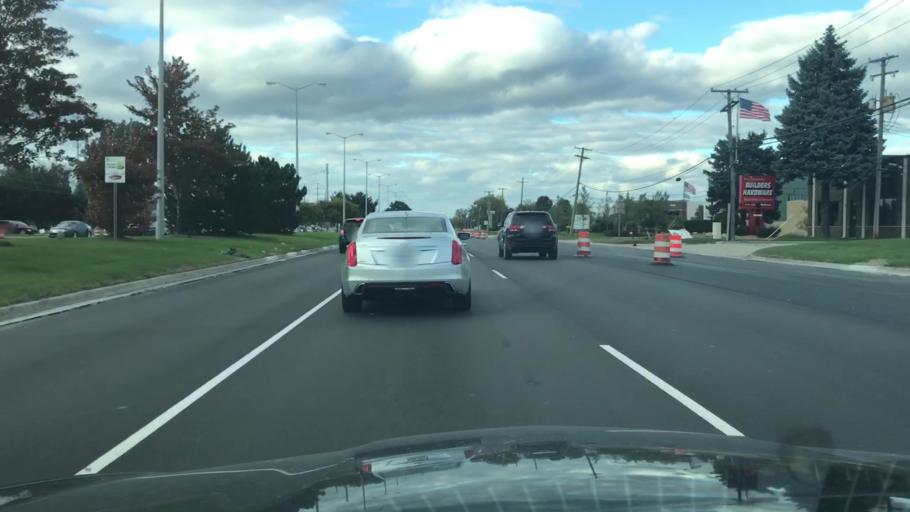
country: US
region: Michigan
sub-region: Macomb County
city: Sterling Heights
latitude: 42.5661
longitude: -83.0491
